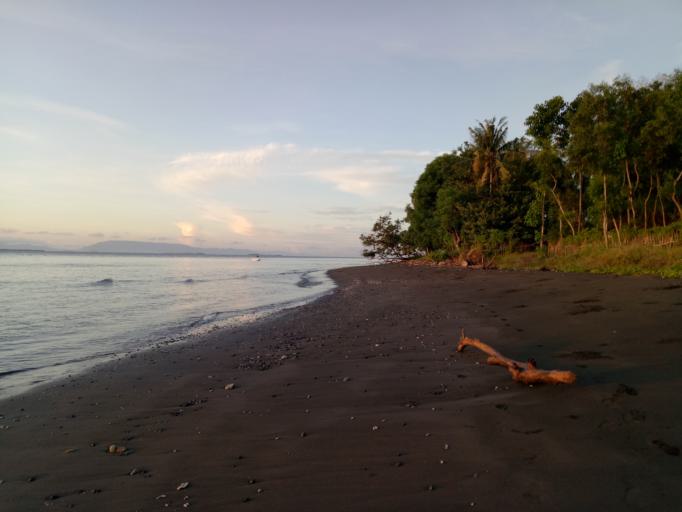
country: ID
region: West Nusa Tenggara
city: Sambelia
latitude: -8.3943
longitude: 116.7227
